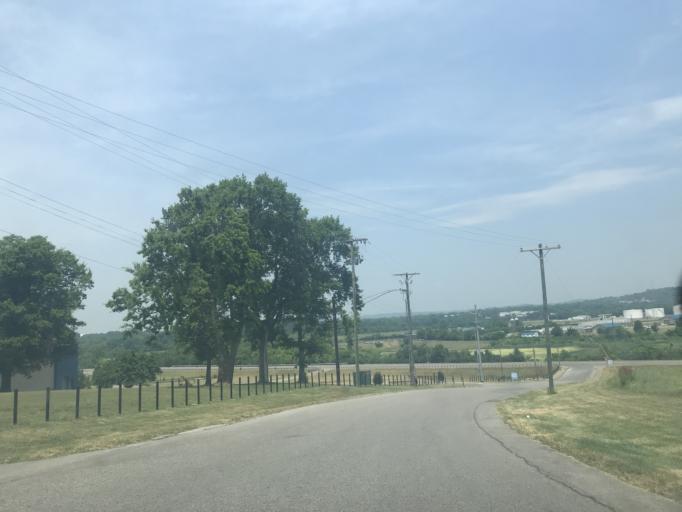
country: US
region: Tennessee
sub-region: Davidson County
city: Nashville
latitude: 36.1709
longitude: -86.8244
